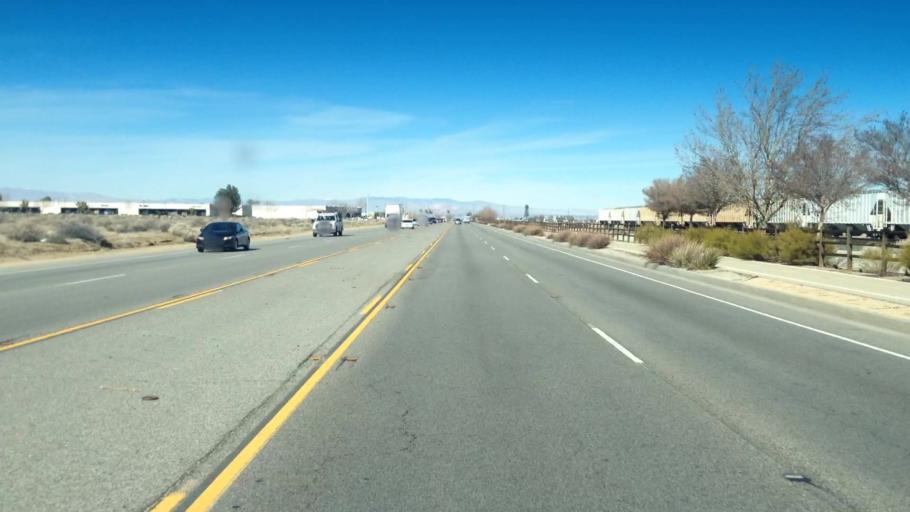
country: US
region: California
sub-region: Los Angeles County
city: Desert View Highlands
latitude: 34.6355
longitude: -118.1266
